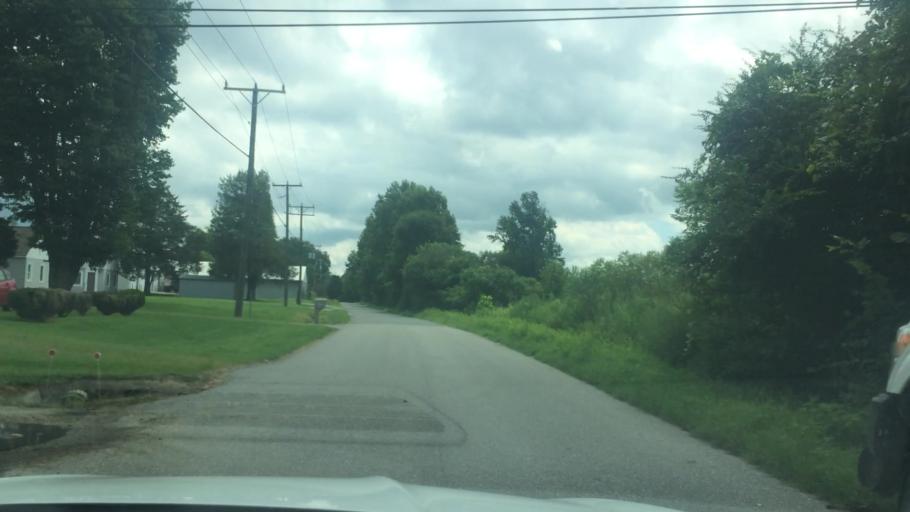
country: US
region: Virginia
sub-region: New Kent County
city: New Kent
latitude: 37.4408
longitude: -77.0377
